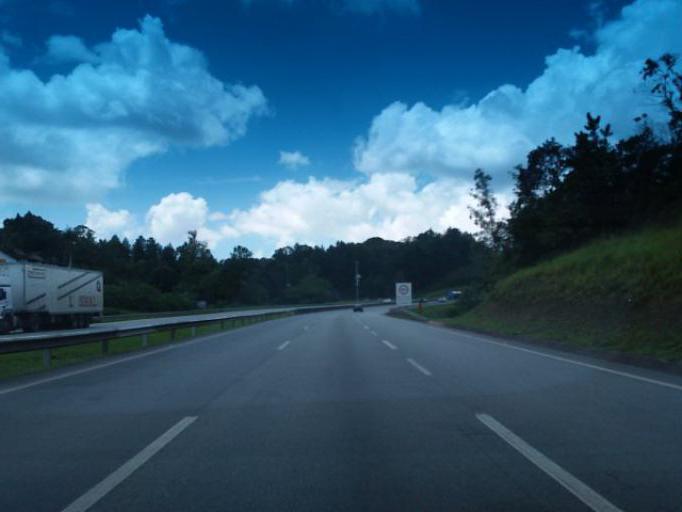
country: BR
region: Sao Paulo
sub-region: Juquitiba
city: Juquitiba
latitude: -24.0071
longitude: -47.1595
